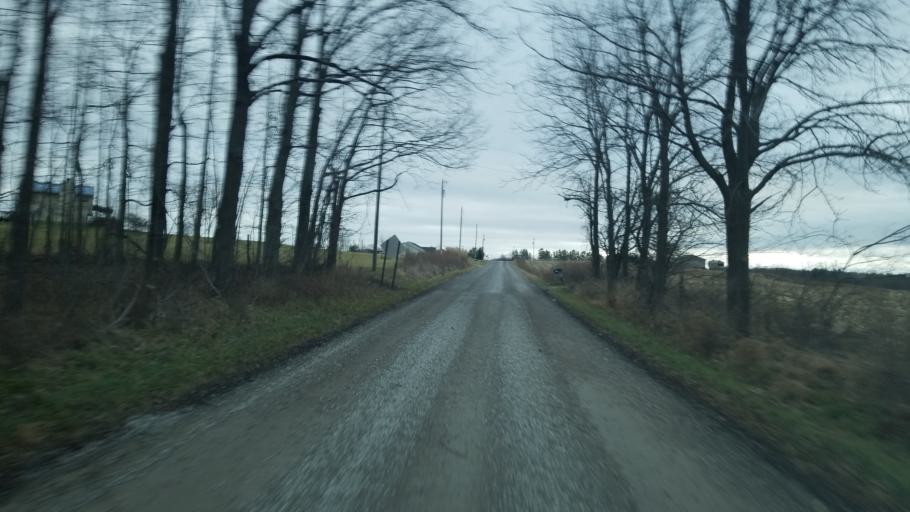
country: US
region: Ohio
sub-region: Knox County
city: Fredericktown
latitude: 40.5027
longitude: -82.6727
